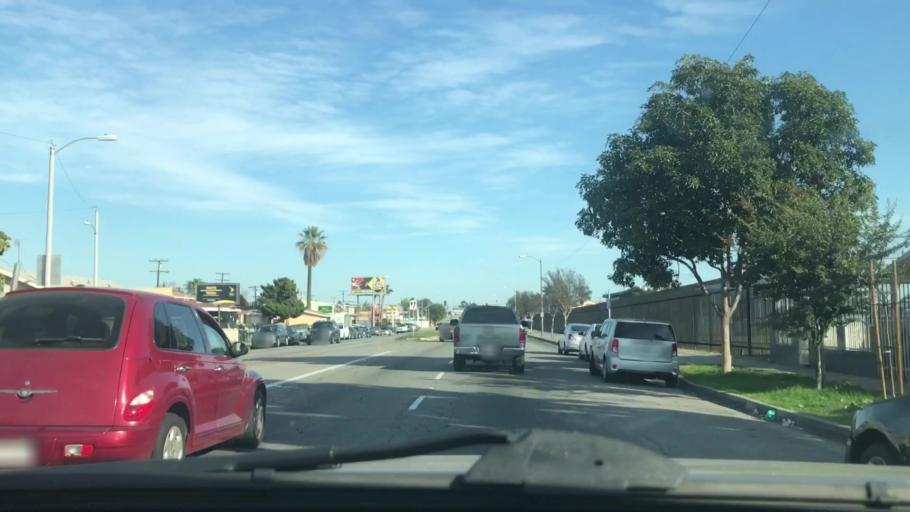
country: US
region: California
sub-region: Los Angeles County
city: East Rancho Dominguez
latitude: 33.9035
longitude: -118.1922
